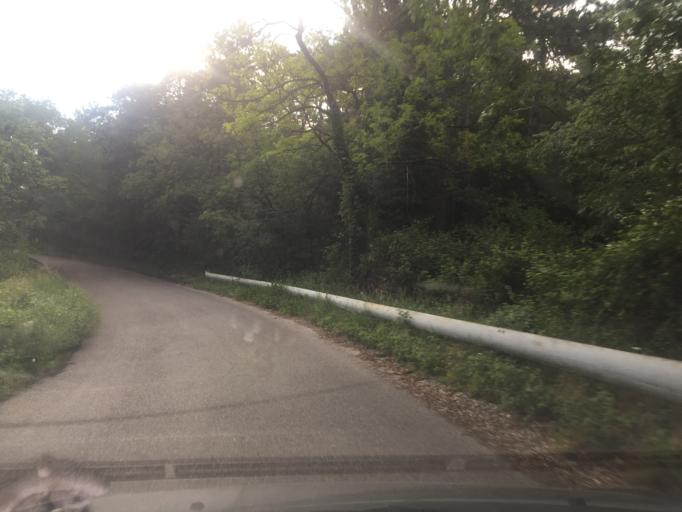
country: IT
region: Friuli Venezia Giulia
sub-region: Provincia di Gorizia
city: Doberdo del Lago
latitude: 45.8756
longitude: 13.5520
